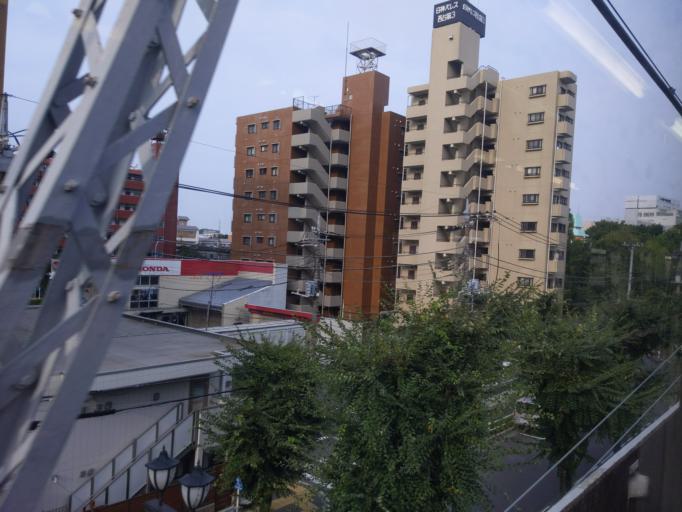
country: JP
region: Saitama
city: Shimotoda
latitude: 35.7873
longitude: 139.6713
